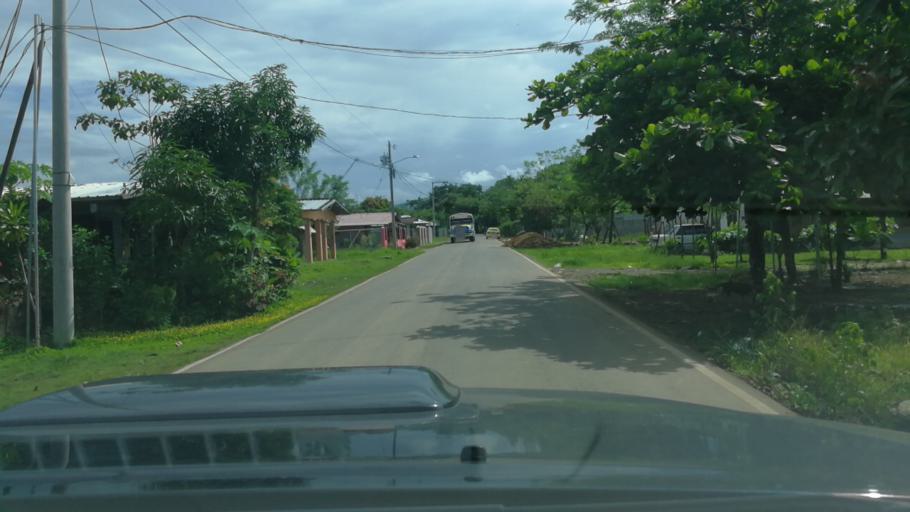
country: PA
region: Panama
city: Paso Blanco
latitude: 9.1356
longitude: -79.2530
